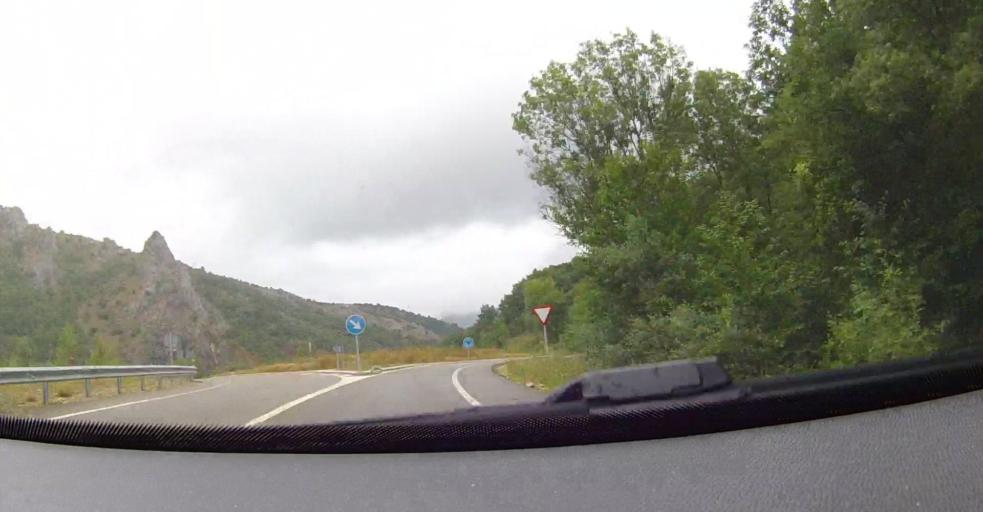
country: ES
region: Castille and Leon
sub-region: Provincia de Leon
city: Cistierna
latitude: 42.8128
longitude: -5.1311
